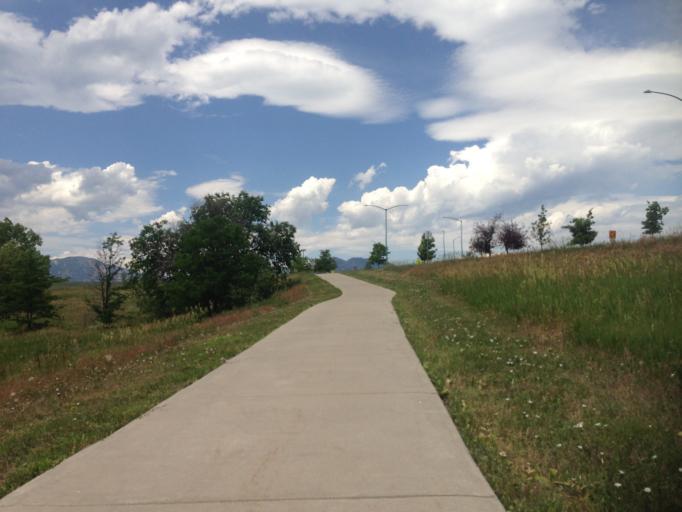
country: US
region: Colorado
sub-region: Boulder County
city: Superior
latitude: 39.9284
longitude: -105.1642
